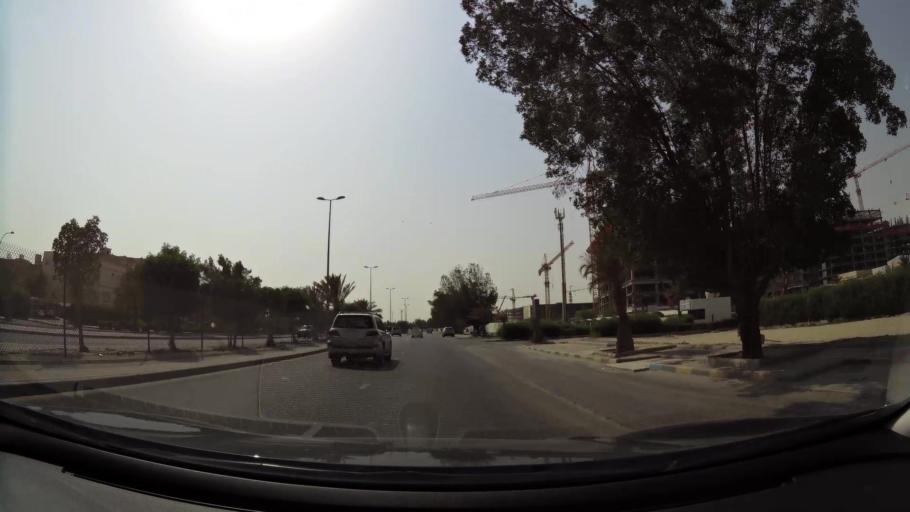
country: KW
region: Muhafazat al Jahra'
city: Al Jahra'
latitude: 29.3379
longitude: 47.6861
